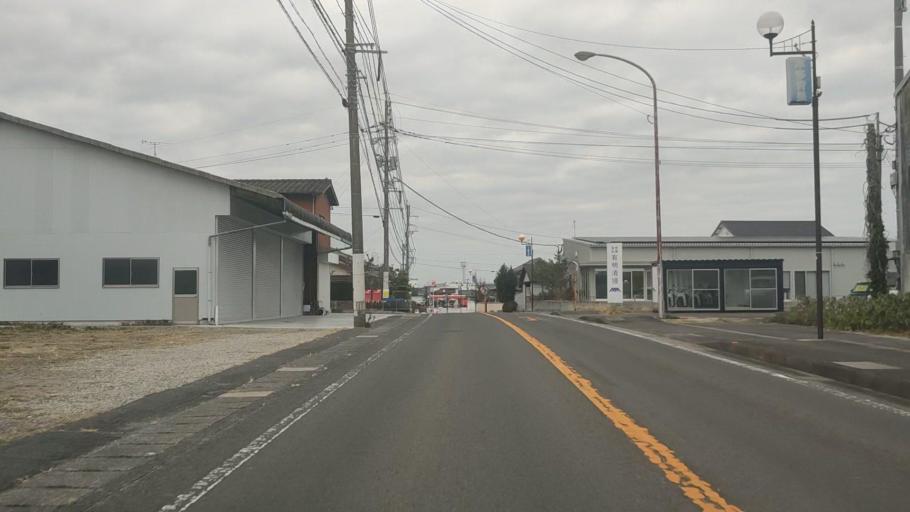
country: JP
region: Nagasaki
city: Shimabara
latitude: 32.8310
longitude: 130.3484
